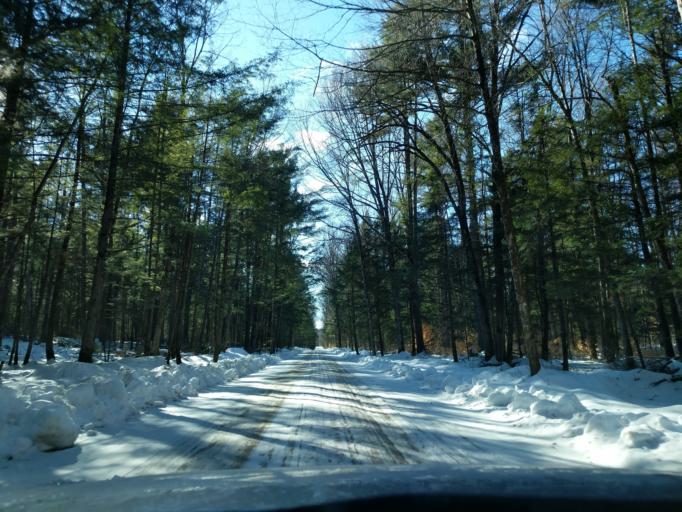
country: US
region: Wisconsin
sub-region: Menominee County
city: Keshena
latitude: 45.0913
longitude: -88.6215
